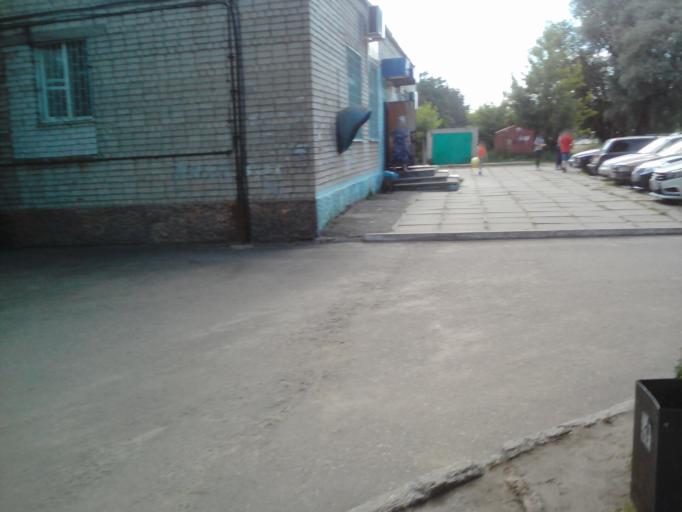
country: RU
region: Kursk
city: Voroshnevo
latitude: 51.6676
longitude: 36.0860
